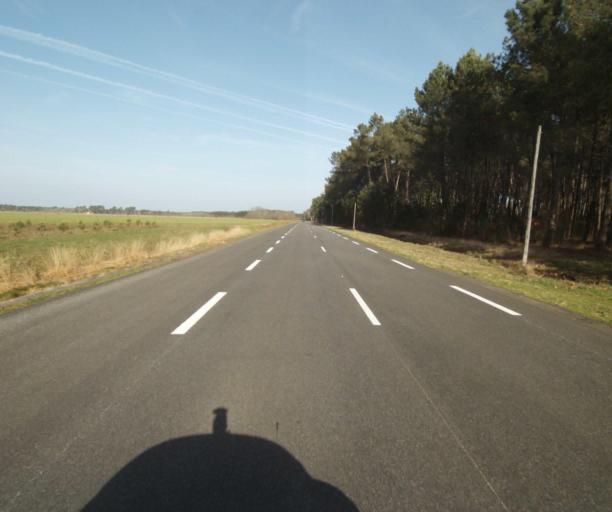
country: FR
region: Aquitaine
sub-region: Departement de la Gironde
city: Grignols
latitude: 44.2013
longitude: -0.1460
